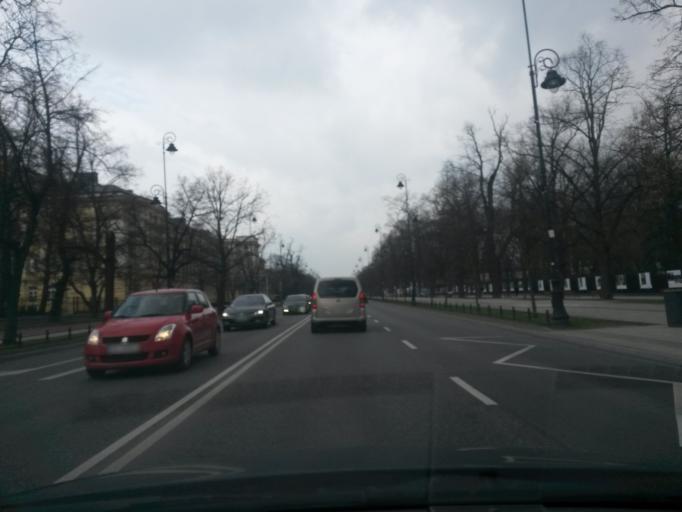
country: PL
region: Masovian Voivodeship
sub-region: Warszawa
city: Srodmiescie
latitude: 52.2143
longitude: 21.0266
